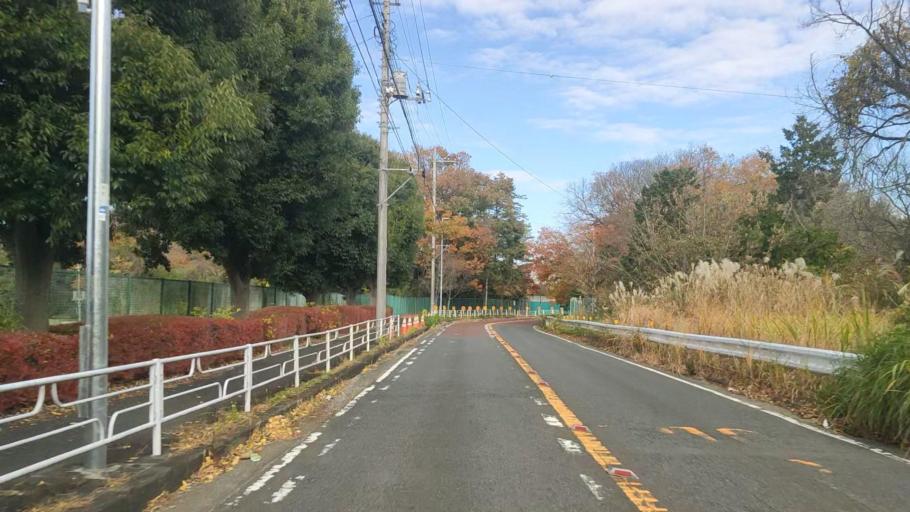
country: JP
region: Kanagawa
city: Minami-rinkan
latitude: 35.4468
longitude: 139.5374
